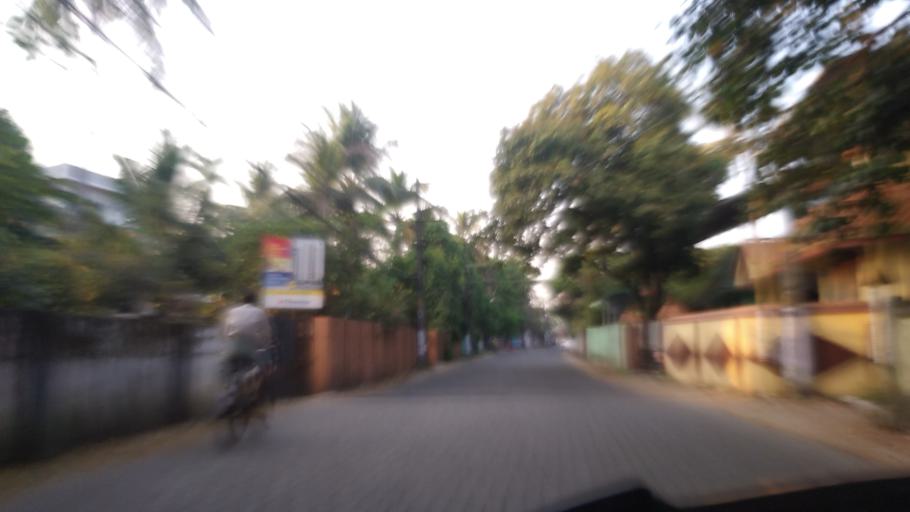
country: IN
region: Kerala
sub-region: Ernakulam
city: Elur
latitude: 10.0312
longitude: 76.2749
